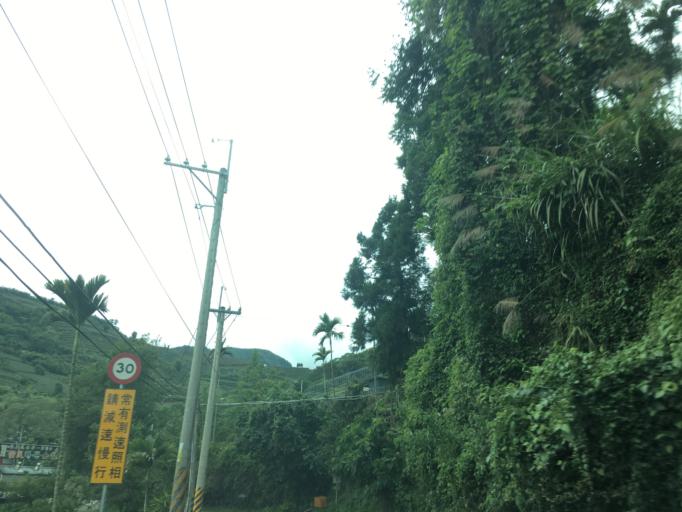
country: TW
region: Taiwan
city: Lugu
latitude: 23.5458
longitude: 120.7060
